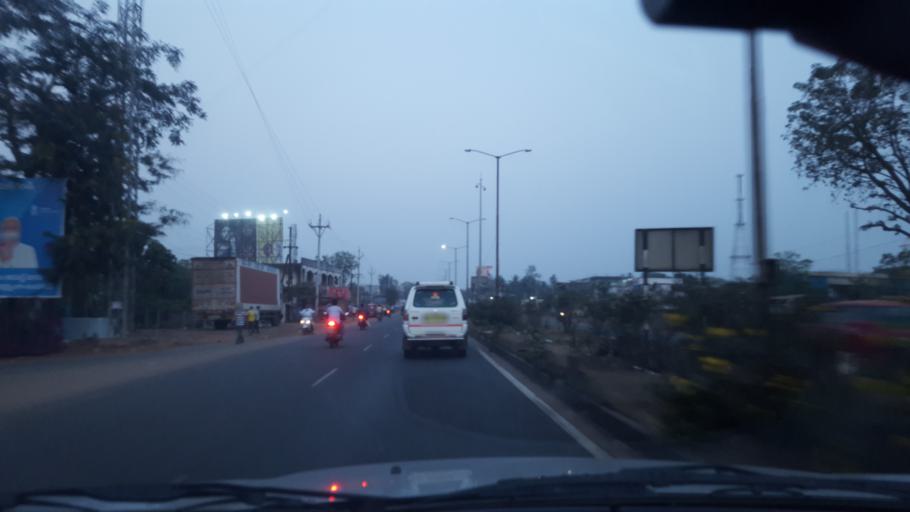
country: IN
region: Andhra Pradesh
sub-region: East Godavari
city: Rajahmundry
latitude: 17.0266
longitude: 81.8079
